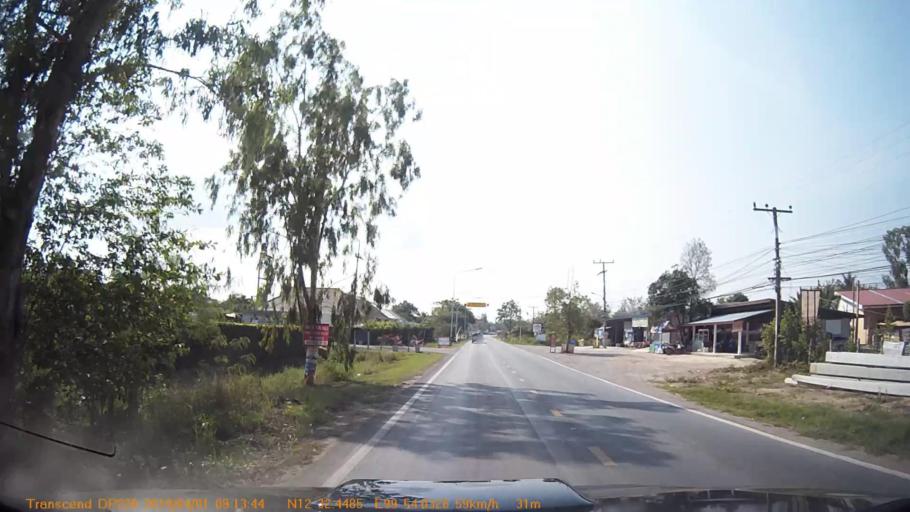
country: TH
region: Prachuap Khiri Khan
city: Hua Hin
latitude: 12.5406
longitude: 99.9007
